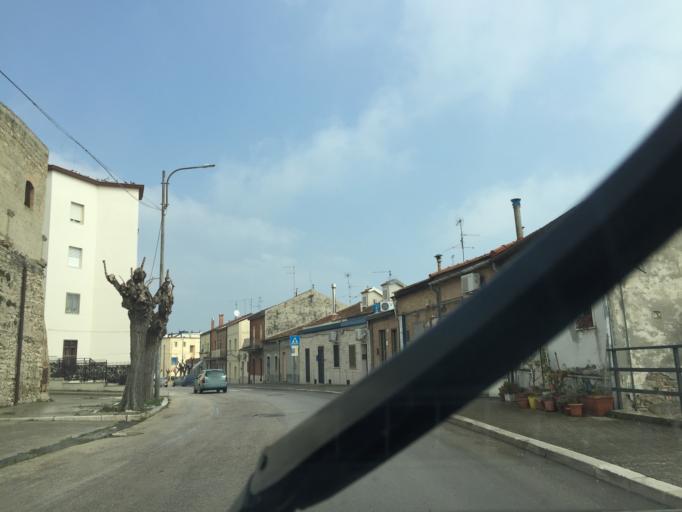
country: IT
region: Apulia
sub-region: Provincia di Foggia
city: Troia
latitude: 41.3624
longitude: 15.3129
